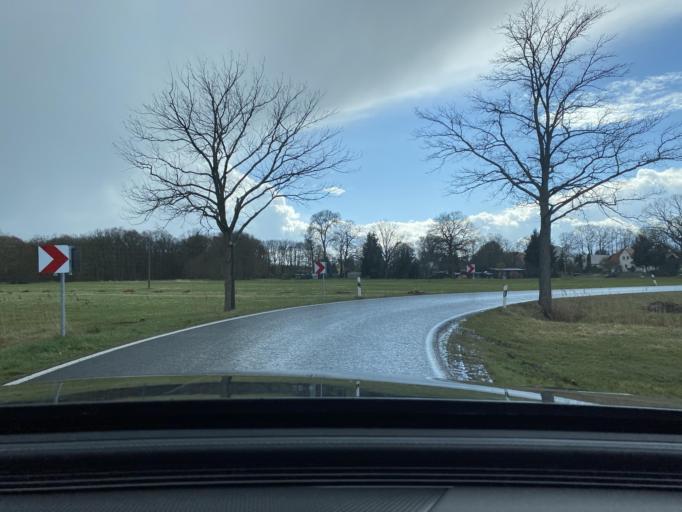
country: DE
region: Saxony
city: Grossdubrau
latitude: 51.3062
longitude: 14.4598
